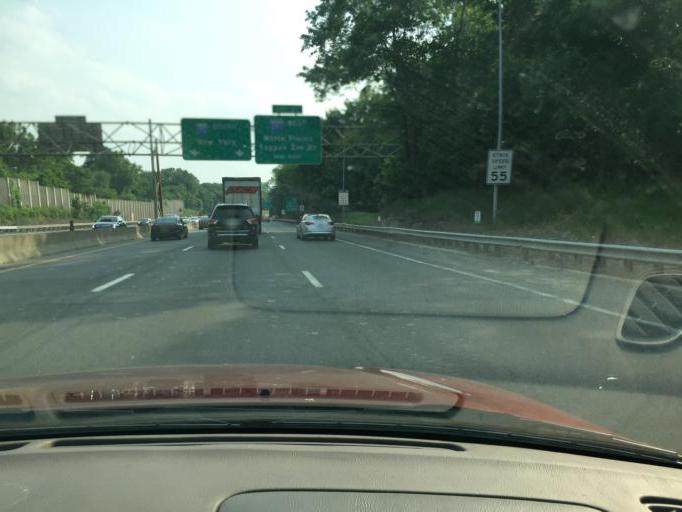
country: US
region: New York
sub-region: Westchester County
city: Port Chester
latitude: 40.9911
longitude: -73.6633
